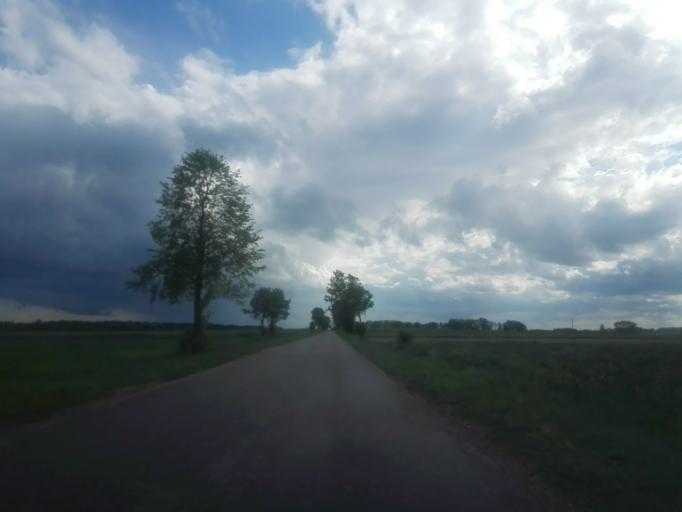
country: PL
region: Podlasie
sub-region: Powiat lomzynski
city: Wizna
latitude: 53.2188
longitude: 22.4139
